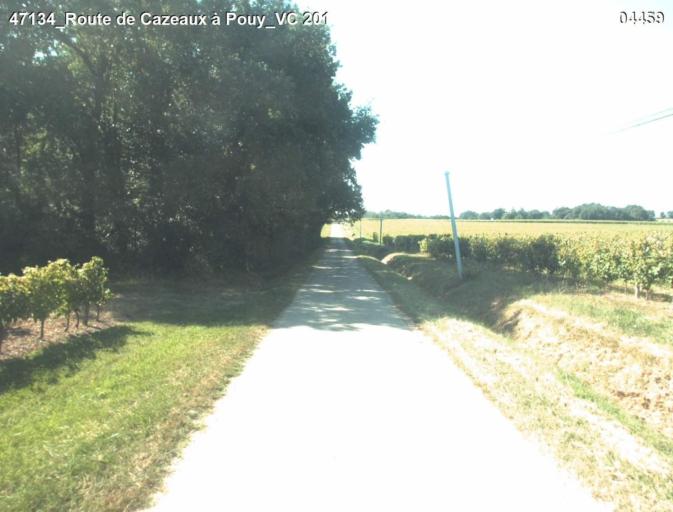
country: FR
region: Aquitaine
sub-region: Departement du Lot-et-Garonne
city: Mezin
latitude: 44.0360
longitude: 0.3121
